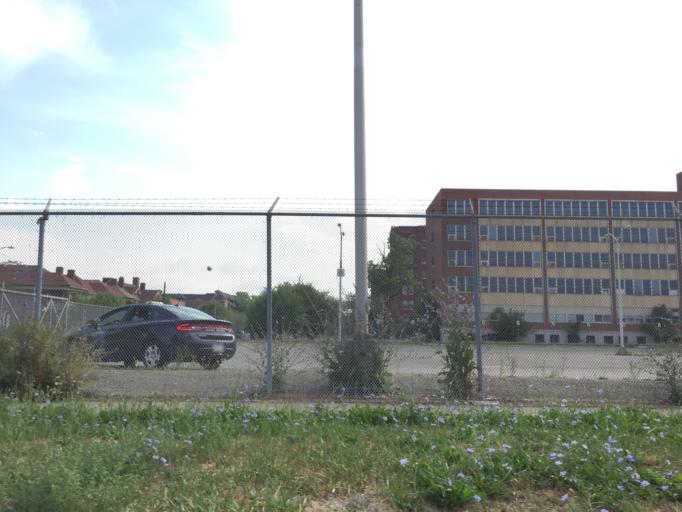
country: US
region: Michigan
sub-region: Wayne County
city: Highland Park
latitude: 42.3775
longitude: -83.0929
